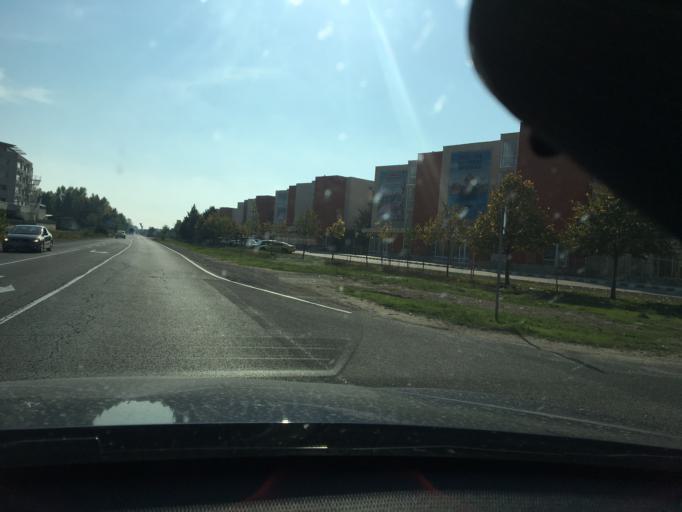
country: BG
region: Burgas
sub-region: Obshtina Nesebur
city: Nesebar
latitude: 42.7014
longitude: 27.7049
